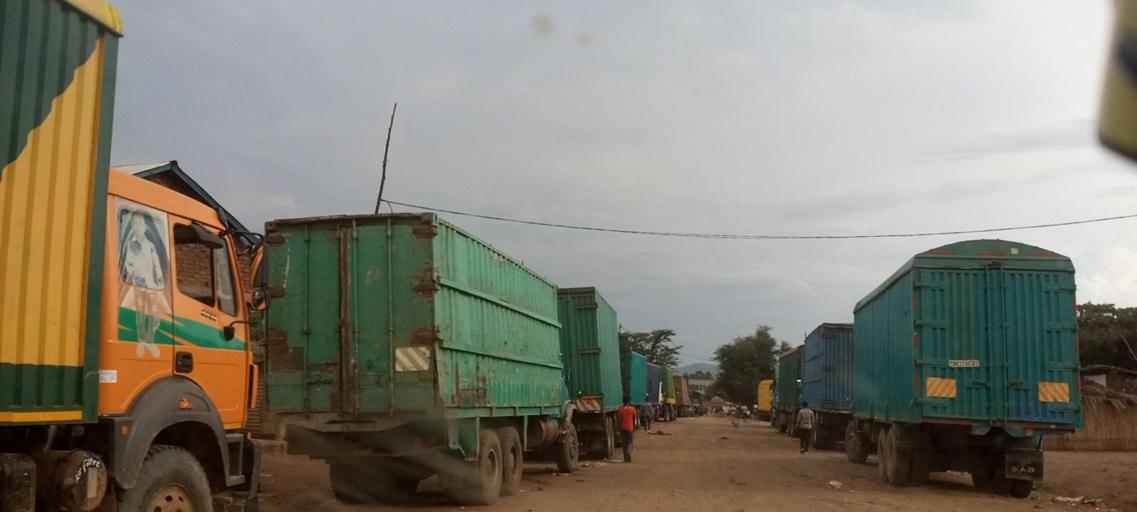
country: BI
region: Cibitoke
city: Cibitoke
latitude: -2.7305
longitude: 29.0023
